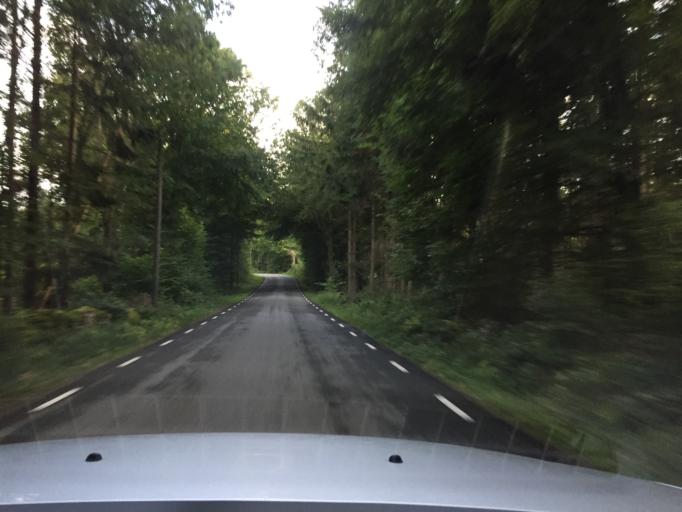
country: SE
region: Skane
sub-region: Hassleholms Kommun
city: Vinslov
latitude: 56.0063
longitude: 13.8174
